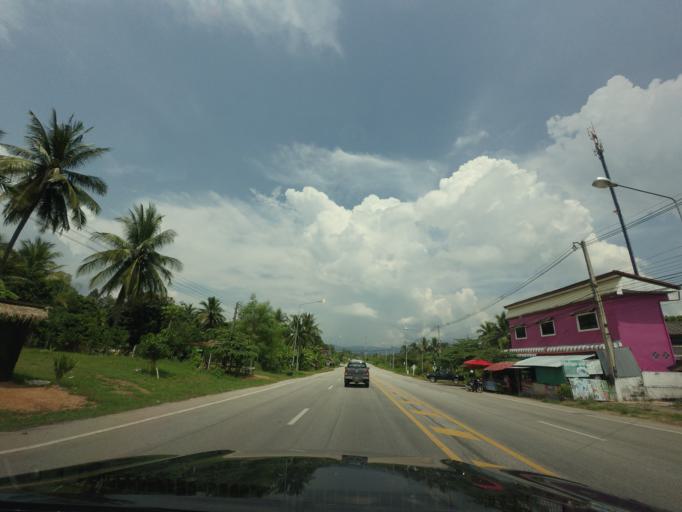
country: TH
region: Khon Kaen
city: Wiang Kao
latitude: 16.6666
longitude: 102.3021
